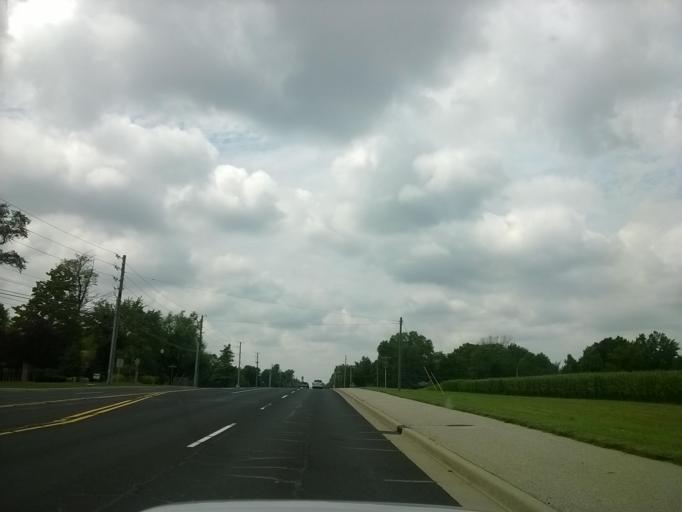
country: US
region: Indiana
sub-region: Hamilton County
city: Fishers
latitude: 39.9271
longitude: -86.0484
